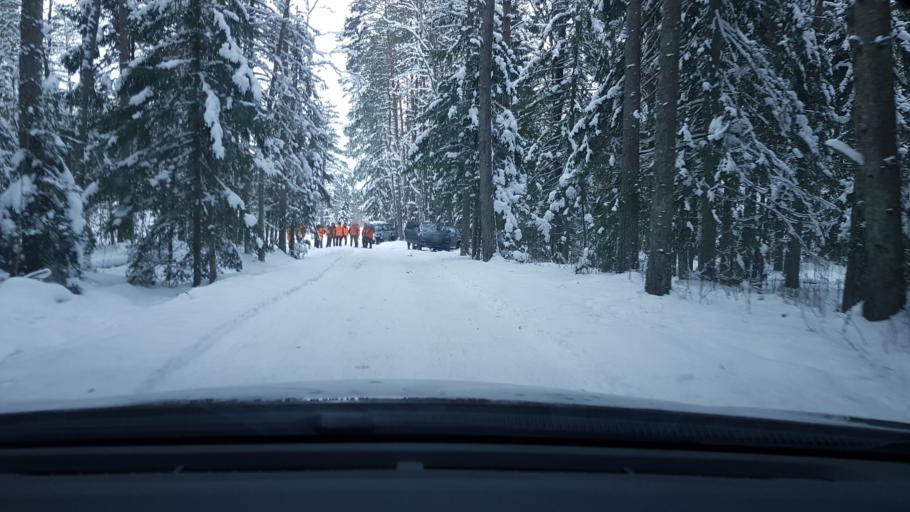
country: EE
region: Harju
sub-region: Harku vald
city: Tabasalu
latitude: 59.4087
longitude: 24.4740
